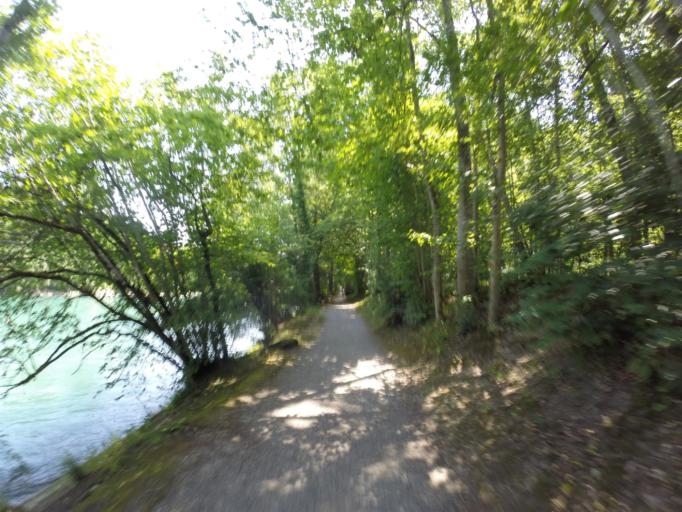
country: CH
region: Bern
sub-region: Bern-Mittelland District
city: Kehrsatz
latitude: 46.9296
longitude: 7.4642
